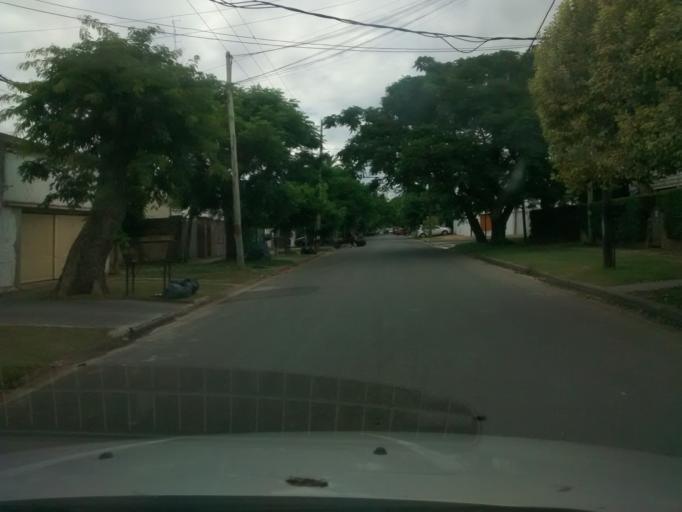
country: AR
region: Buenos Aires
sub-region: Partido de La Plata
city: La Plata
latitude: -34.9200
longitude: -57.9117
